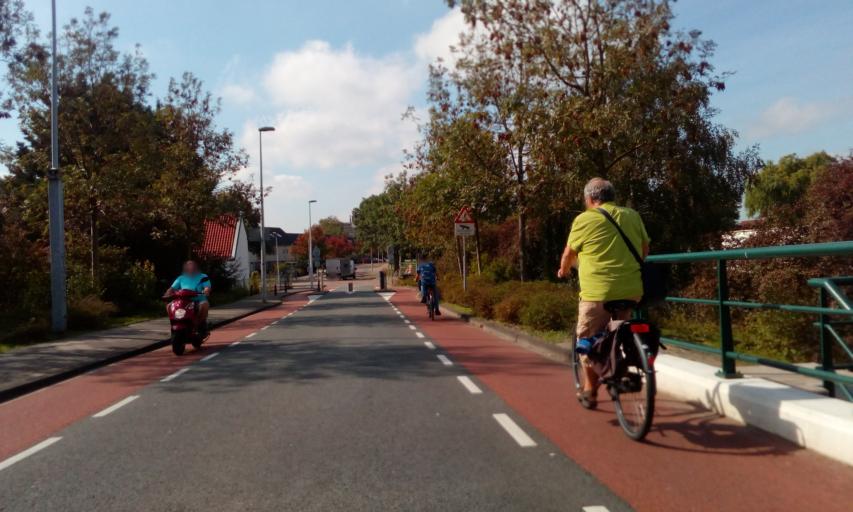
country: NL
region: South Holland
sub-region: Gemeente Oegstgeest
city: Oegstgeest
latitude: 52.1562
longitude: 4.4552
